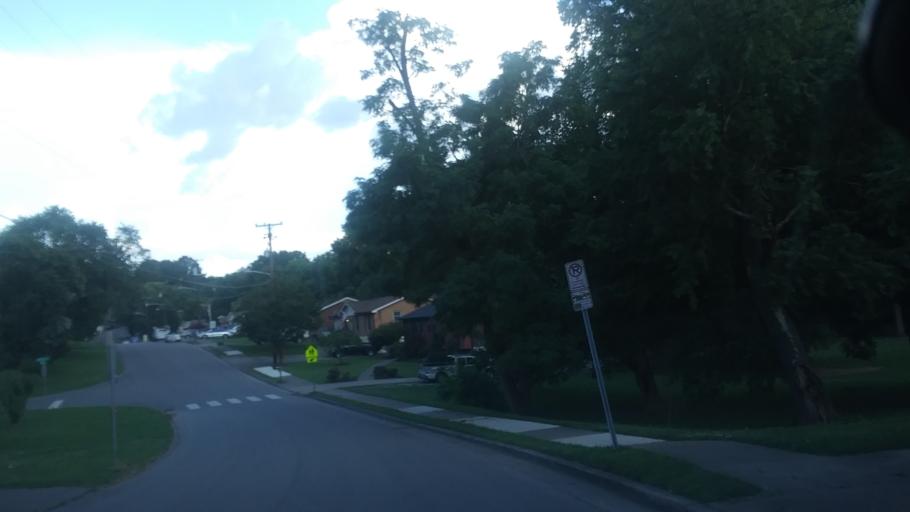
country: US
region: Tennessee
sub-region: Rutherford County
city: La Vergne
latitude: 36.0666
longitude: -86.6689
